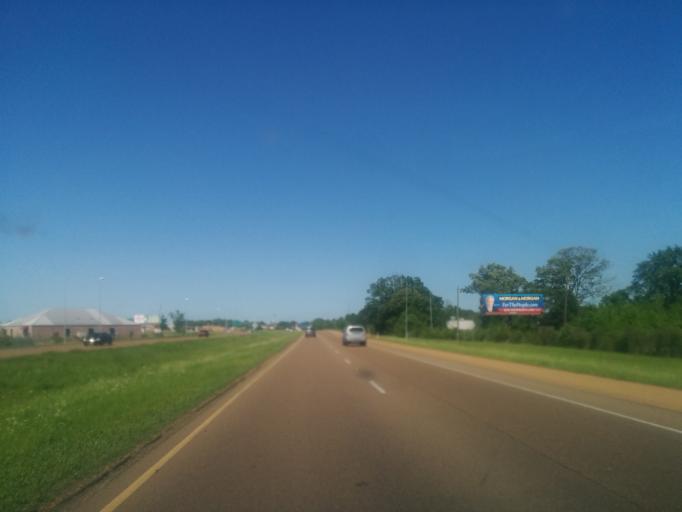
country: US
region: Mississippi
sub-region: Madison County
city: Madison
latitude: 32.5098
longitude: -90.1080
